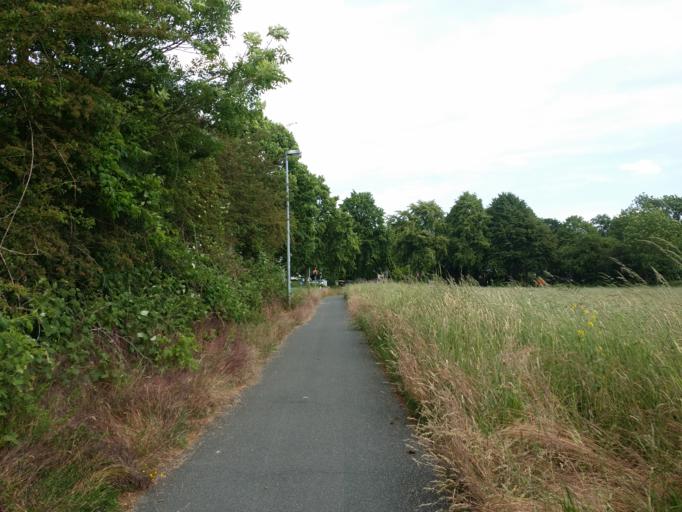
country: DE
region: Lower Saxony
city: Riede
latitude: 53.0134
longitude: 8.8815
